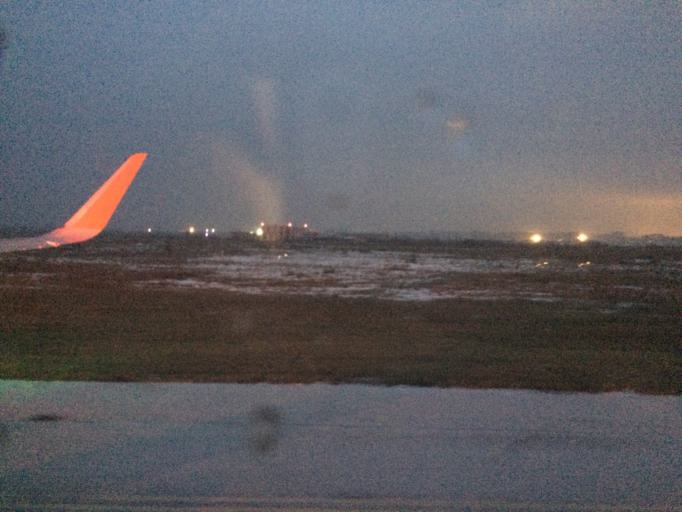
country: RU
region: Novosibirsk
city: Ob'
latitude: 55.0134
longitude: 82.6769
